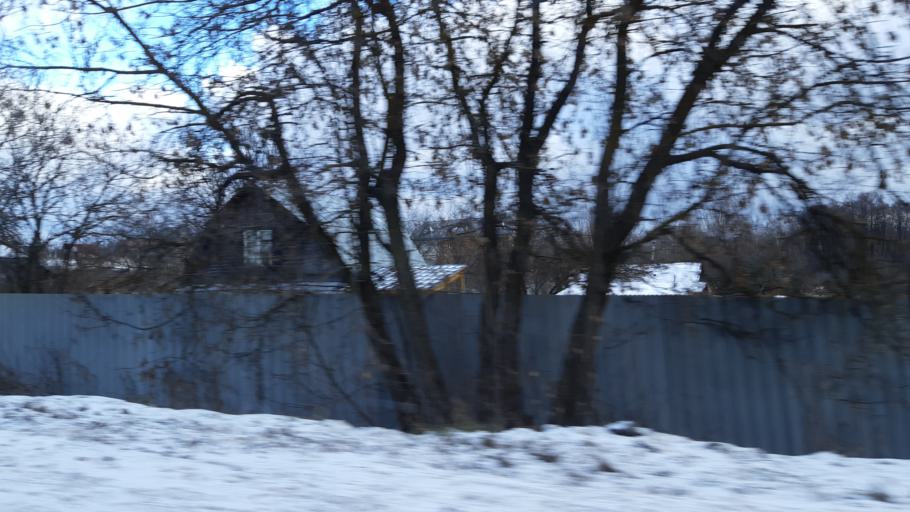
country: RU
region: Moskovskaya
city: Noginsk-9
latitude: 55.9855
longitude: 38.5434
